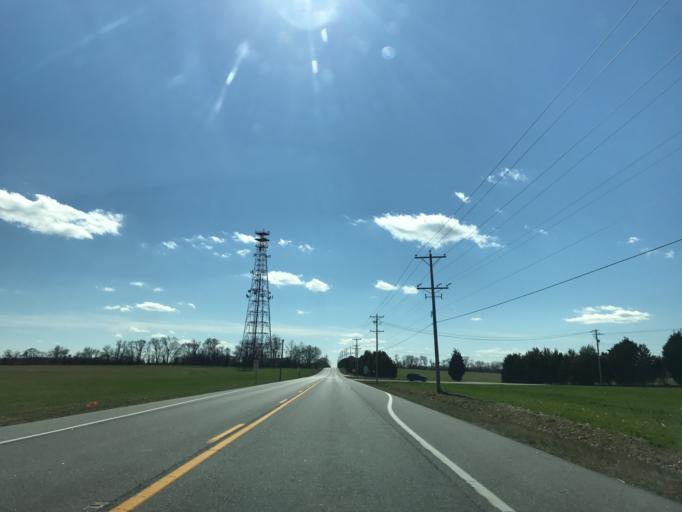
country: US
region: Maryland
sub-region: Kent County
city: Rock Hall
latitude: 39.2142
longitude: -76.1735
